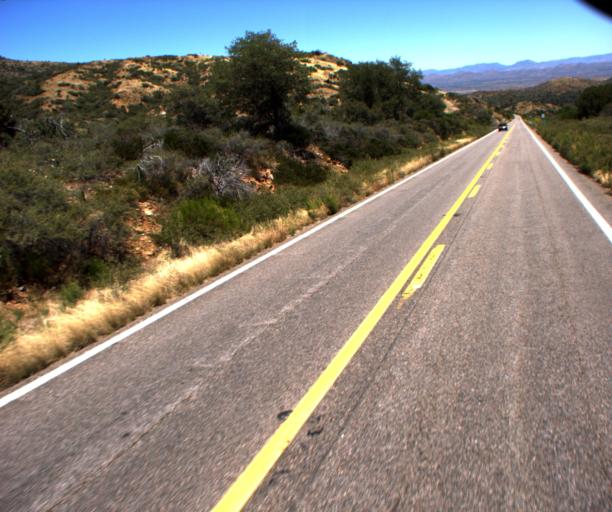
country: US
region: Arizona
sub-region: Gila County
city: Globe
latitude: 33.2781
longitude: -110.7562
